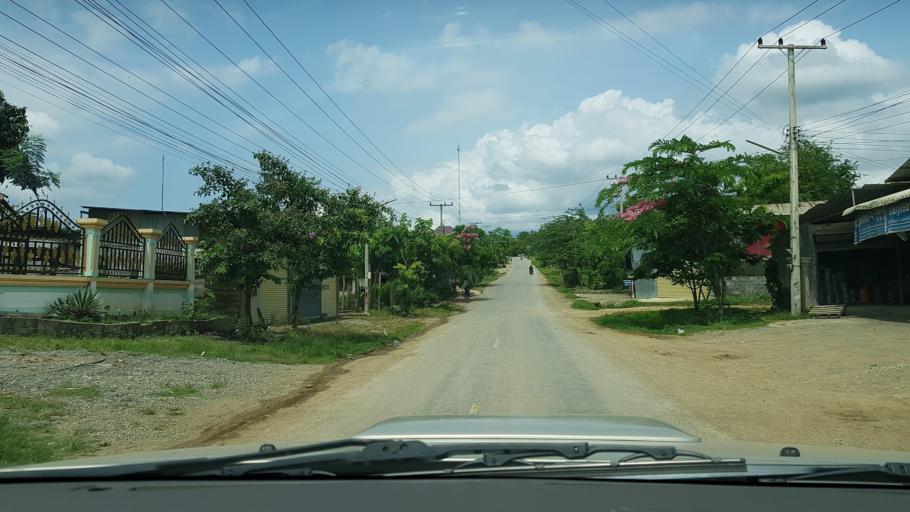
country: LA
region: Loungnamtha
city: Muang Nale
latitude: 20.0274
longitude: 101.3402
